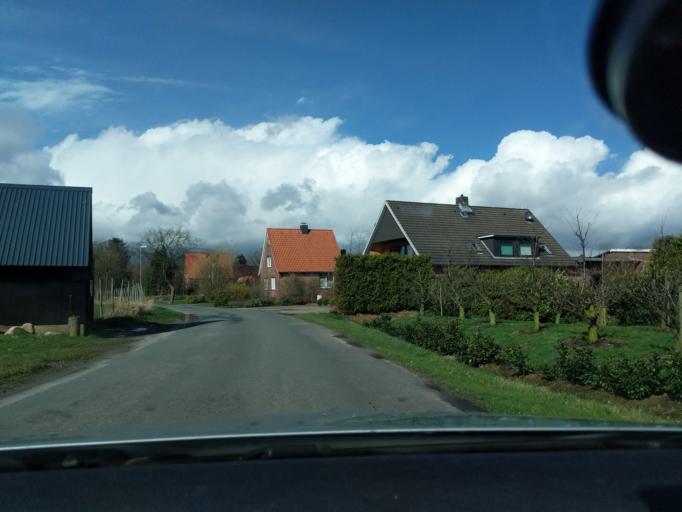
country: DE
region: Lower Saxony
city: Stade
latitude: 53.6098
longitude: 9.5120
